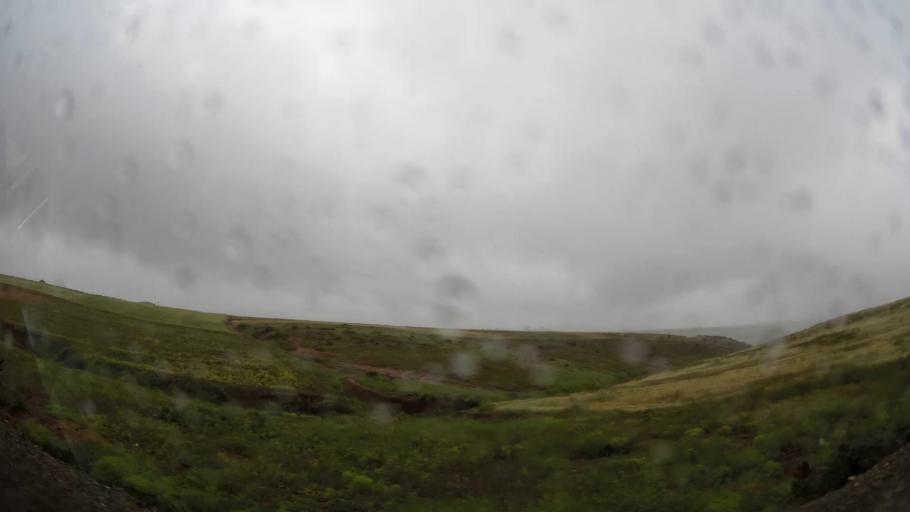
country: MA
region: Oriental
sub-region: Nador
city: Boudinar
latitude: 35.1281
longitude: -3.6293
